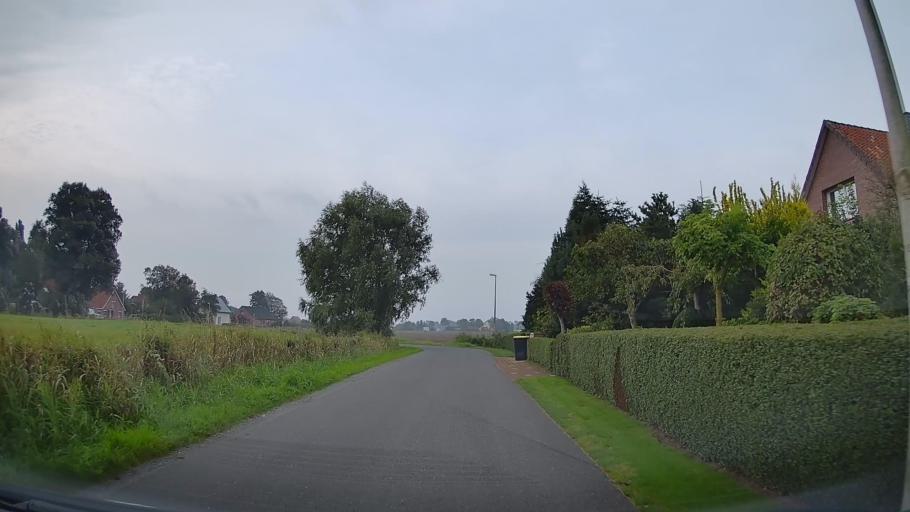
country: DE
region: Lower Saxony
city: Cuxhaven
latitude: 53.8317
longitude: 8.7603
